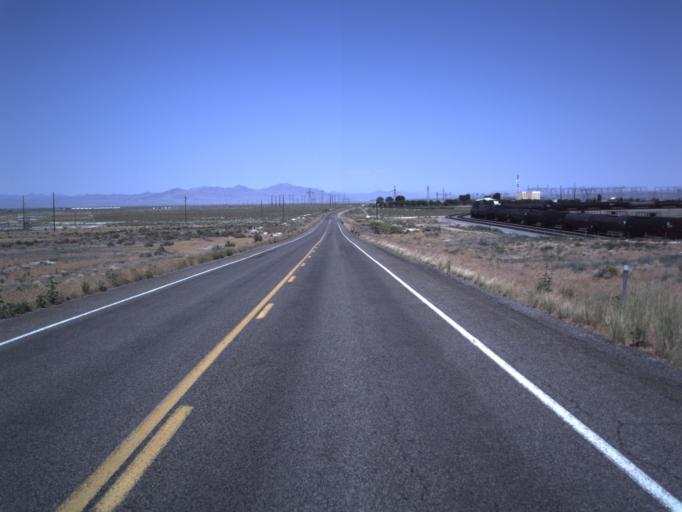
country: US
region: Utah
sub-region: Millard County
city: Delta
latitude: 39.4905
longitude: -112.5581
